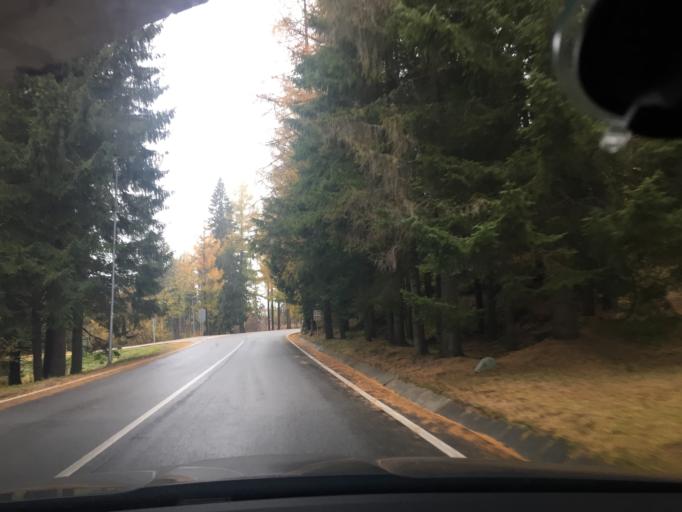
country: SK
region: Presovsky
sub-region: Okres Poprad
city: Strba
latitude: 49.1184
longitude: 20.0687
